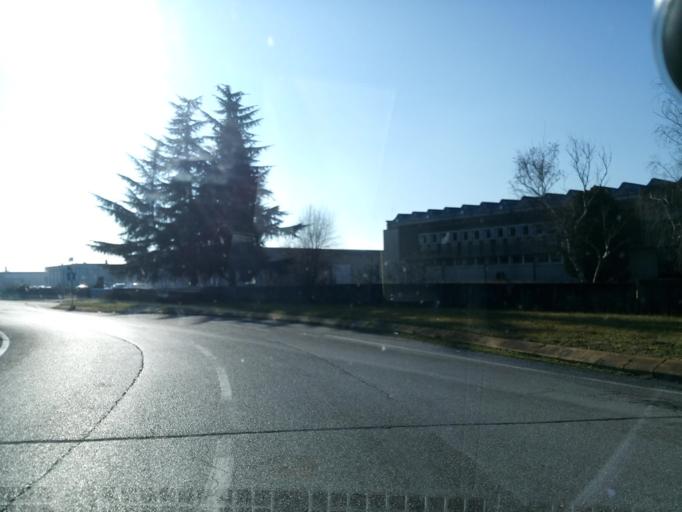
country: IT
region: Veneto
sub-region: Provincia di Treviso
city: Lancenigo-Villorba
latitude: 45.7304
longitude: 12.2475
